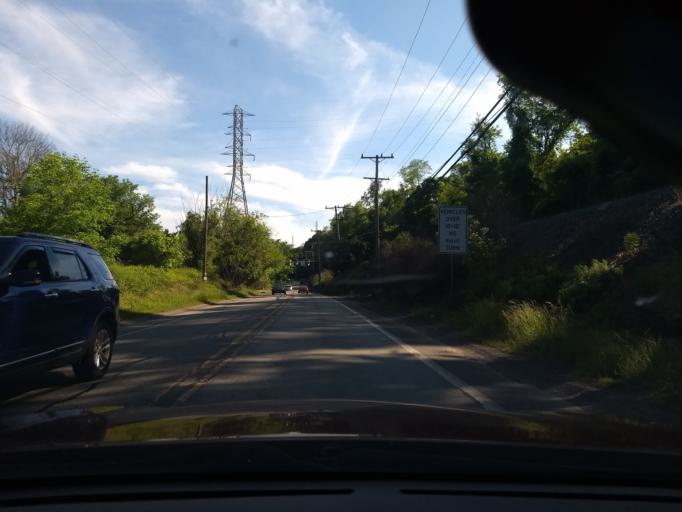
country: US
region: Pennsylvania
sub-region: Allegheny County
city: Glassport
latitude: 40.3388
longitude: -79.8946
